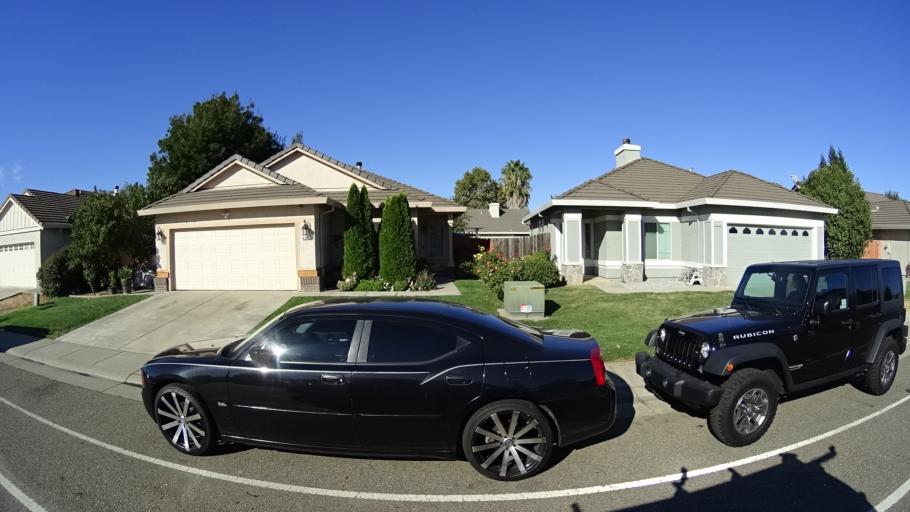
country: US
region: California
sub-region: Sacramento County
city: Elk Grove
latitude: 38.4442
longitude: -121.3864
